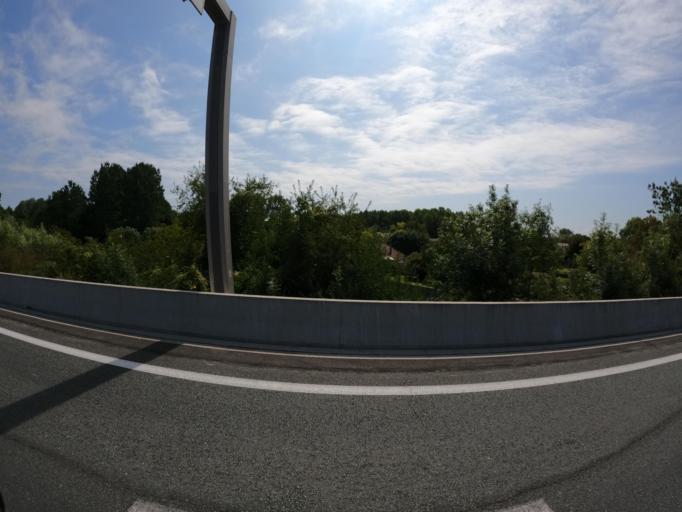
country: FR
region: Poitou-Charentes
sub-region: Departement des Deux-Sevres
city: Frontenay-Rohan-Rohan
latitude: 46.2350
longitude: -0.5847
